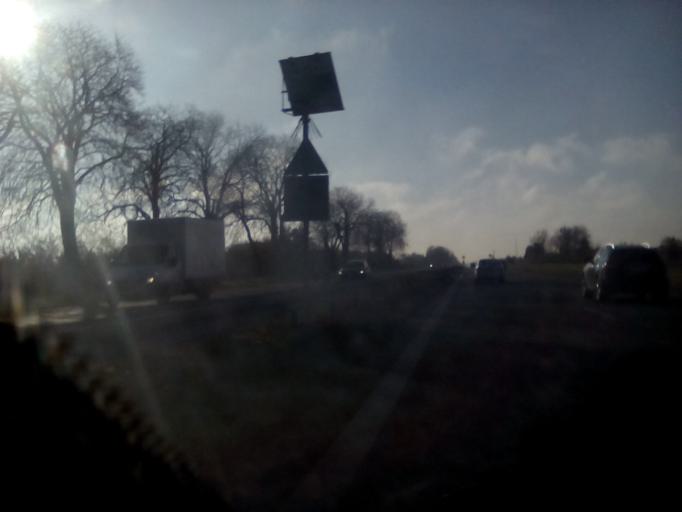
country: PL
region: Masovian Voivodeship
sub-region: Powiat piaseczynski
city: Tarczyn
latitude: 51.9381
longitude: 20.8465
